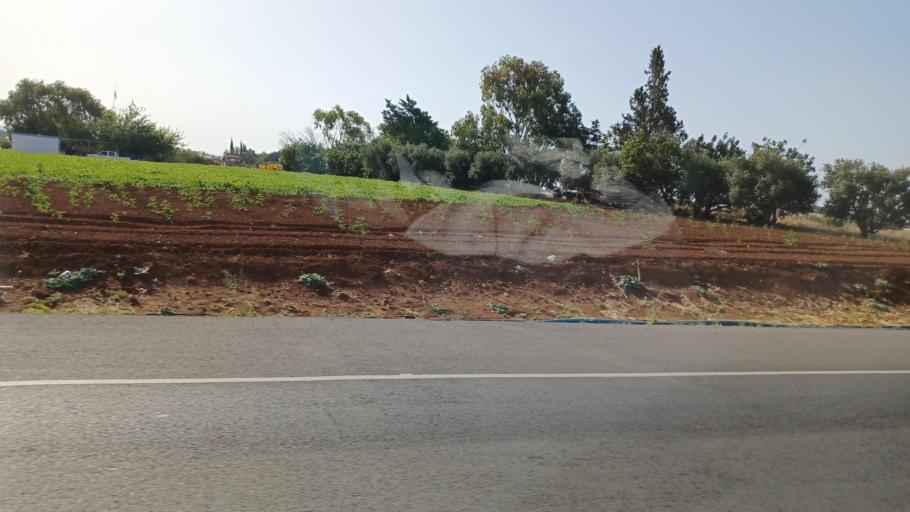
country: CY
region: Ammochostos
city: Liopetri
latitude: 34.9940
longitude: 33.9318
